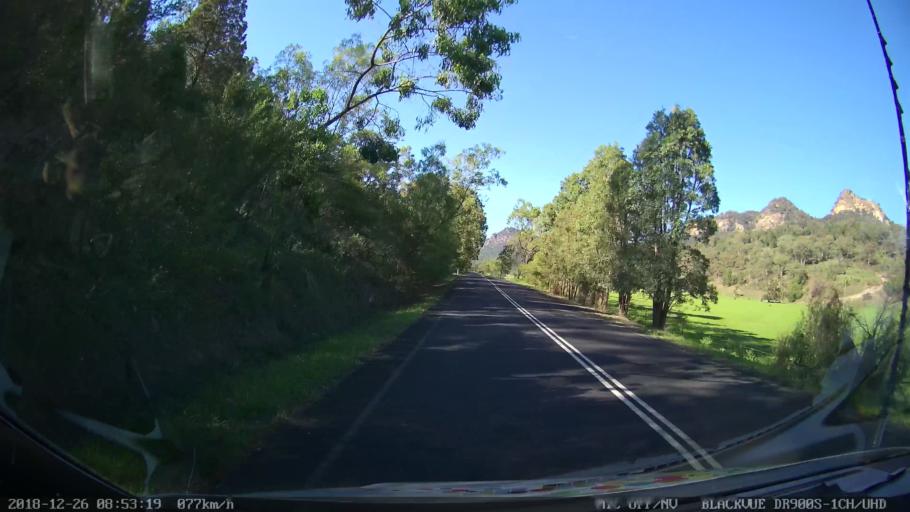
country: AU
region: New South Wales
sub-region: Mid-Western Regional
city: Kandos
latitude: -32.6029
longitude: 150.0782
